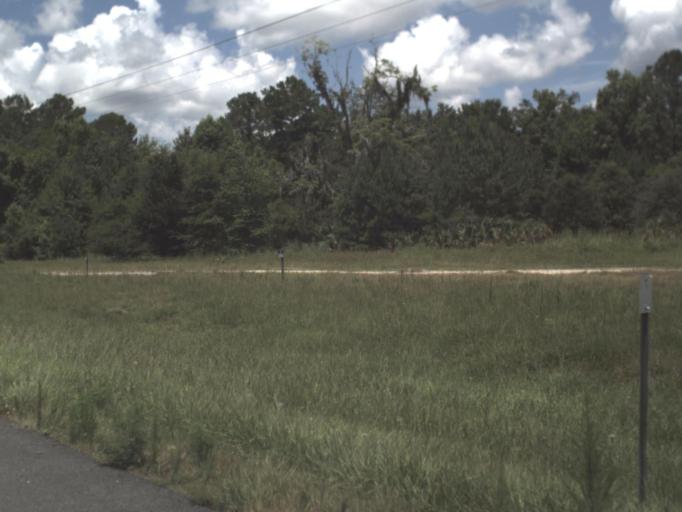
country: US
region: Florida
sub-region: Taylor County
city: Perry
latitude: 30.0843
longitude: -83.6615
